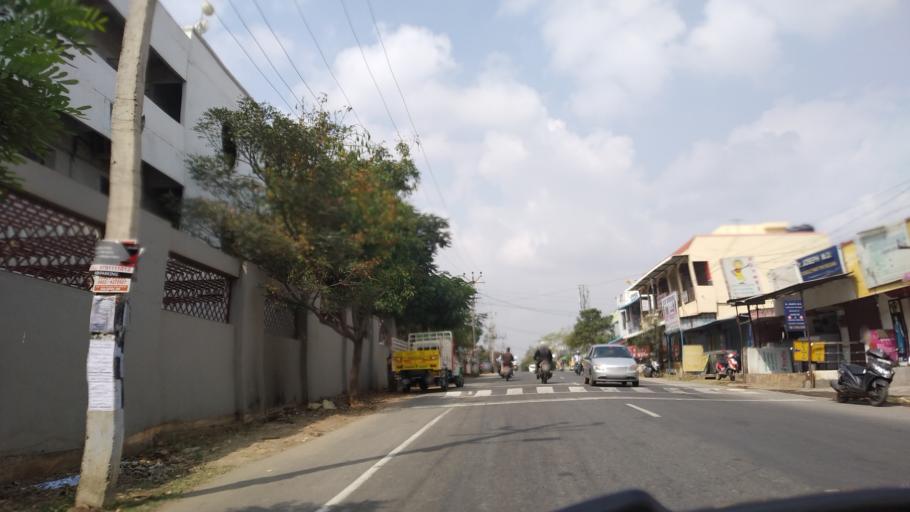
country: IN
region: Tamil Nadu
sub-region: Coimbatore
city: Madukkarai
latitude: 10.9395
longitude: 76.9459
